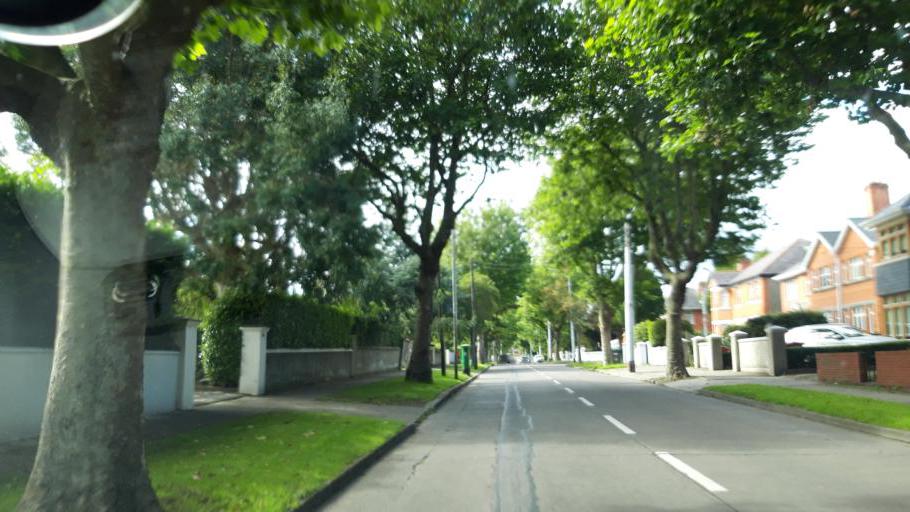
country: IE
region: Leinster
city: Dollymount
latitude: 53.3664
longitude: -6.1882
